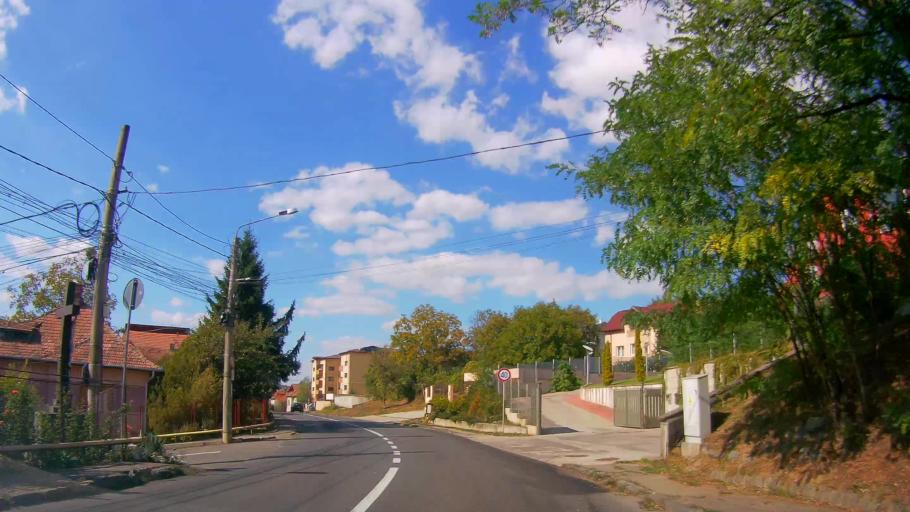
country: RO
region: Salaj
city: Zalau
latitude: 47.1779
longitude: 23.0651
